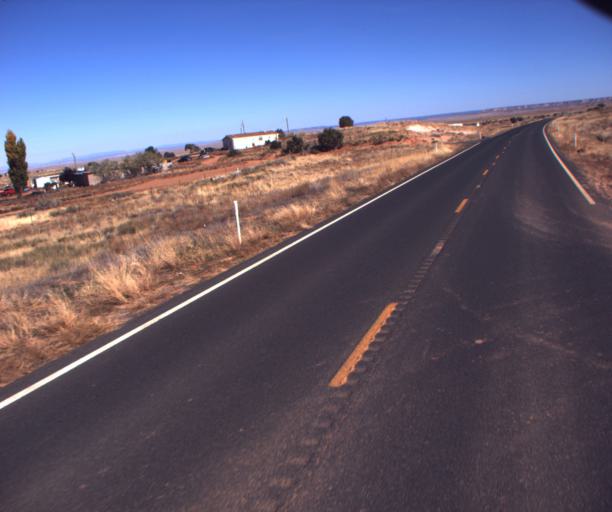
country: US
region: Arizona
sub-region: Apache County
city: Ganado
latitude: 35.7833
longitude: -109.7157
